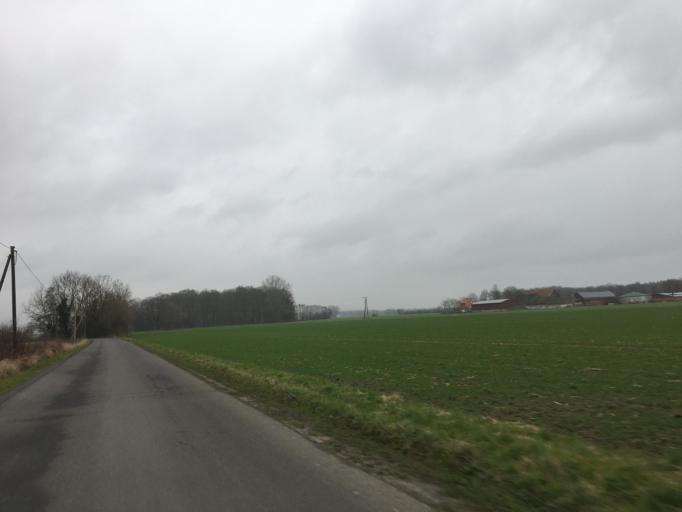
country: DE
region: North Rhine-Westphalia
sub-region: Regierungsbezirk Munster
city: Senden
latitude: 51.8626
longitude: 7.4604
